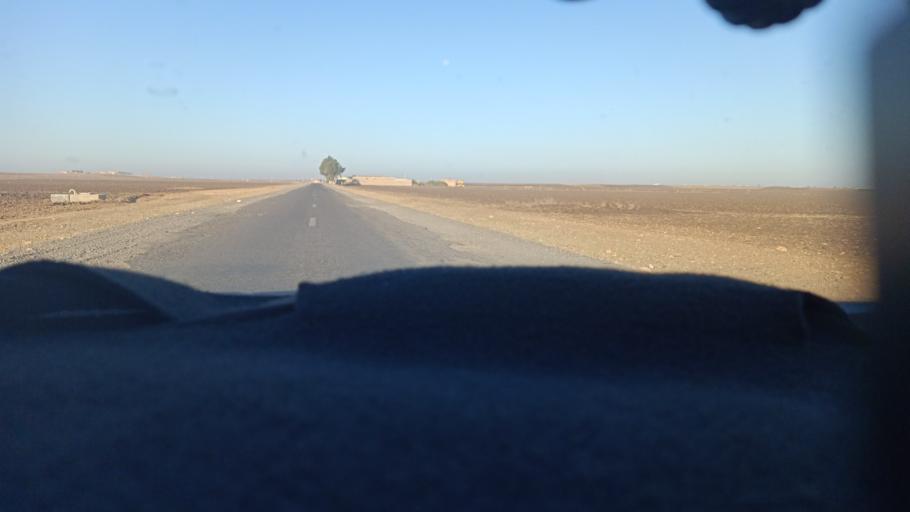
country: MA
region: Doukkala-Abda
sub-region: Safi
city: Youssoufia
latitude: 32.3714
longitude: -8.7128
